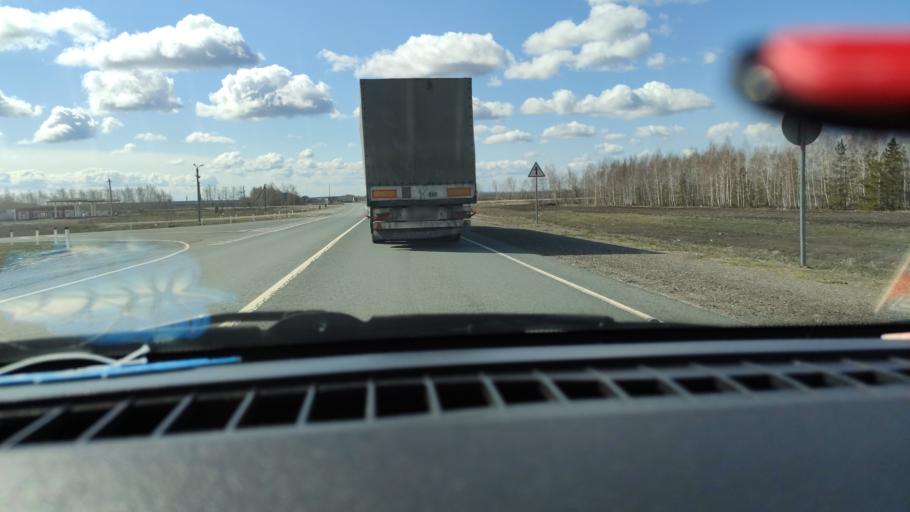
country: RU
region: Samara
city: Syzran'
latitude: 52.9238
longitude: 48.3035
